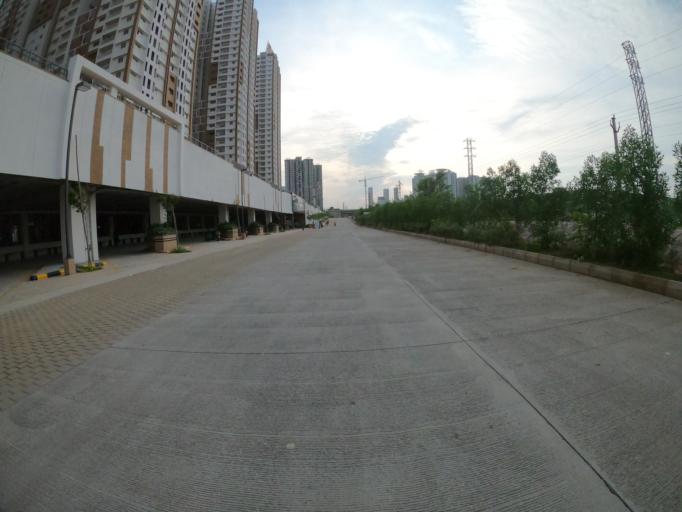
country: IN
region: Telangana
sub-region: Hyderabad
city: Hyderabad
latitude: 17.3997
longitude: 78.3558
